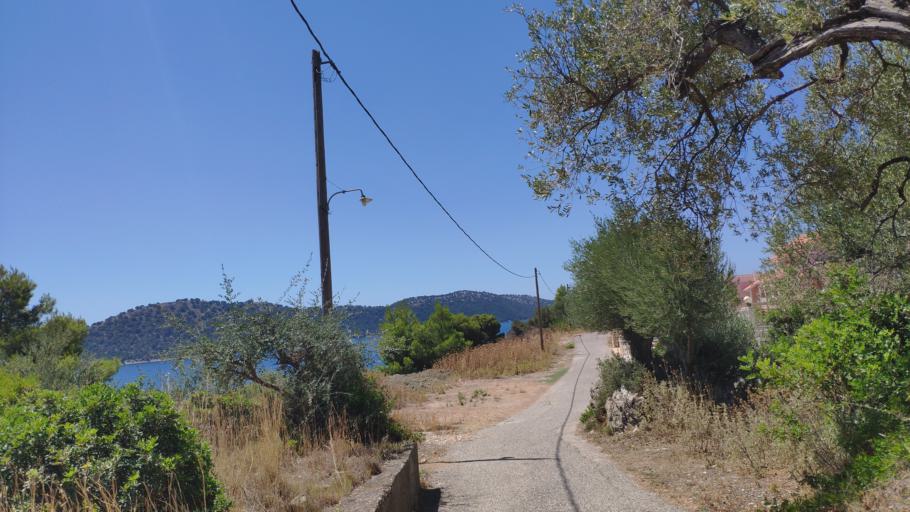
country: GR
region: West Greece
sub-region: Nomos Aitolias kai Akarnanias
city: Kandila
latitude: 38.6180
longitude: 20.9288
